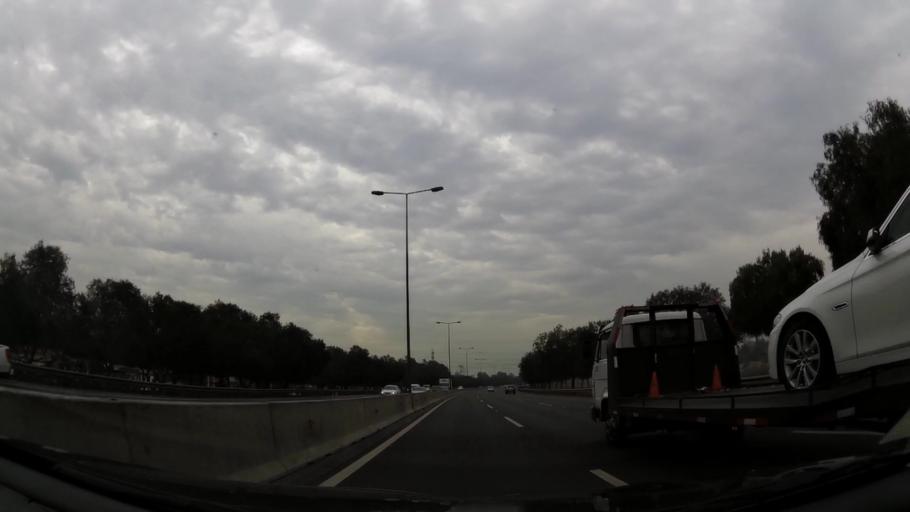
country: CL
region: Santiago Metropolitan
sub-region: Provincia de Santiago
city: Lo Prado
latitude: -33.4116
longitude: -70.7354
